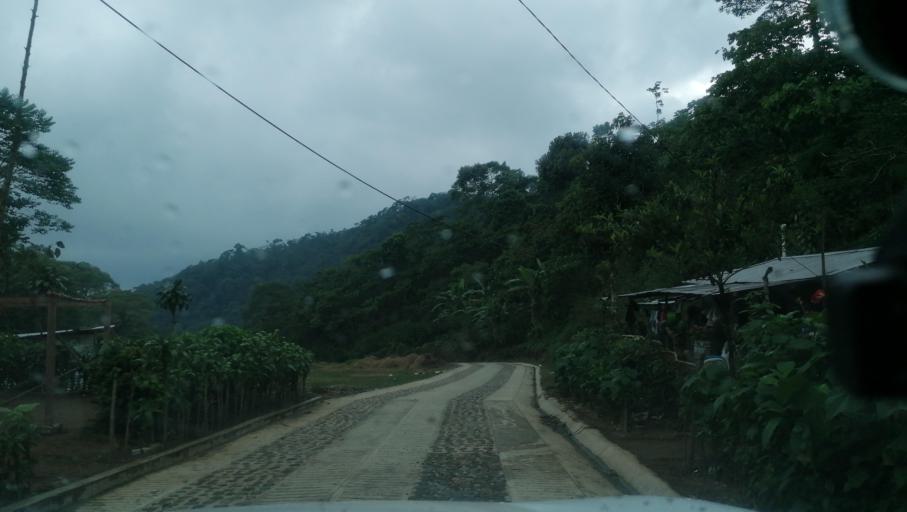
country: MX
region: Chiapas
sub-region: Cacahoatan
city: Benito Juarez
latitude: 15.0963
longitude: -92.1570
